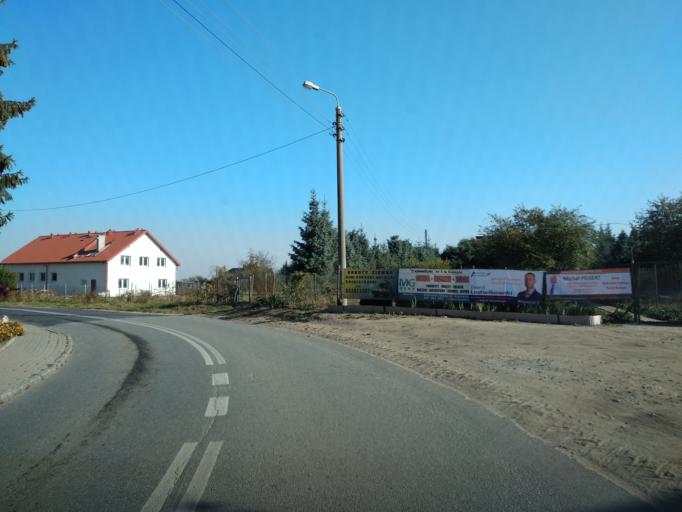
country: PL
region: Lower Silesian Voivodeship
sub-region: Powiat wroclawski
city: Smolec
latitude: 51.0745
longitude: 16.9195
